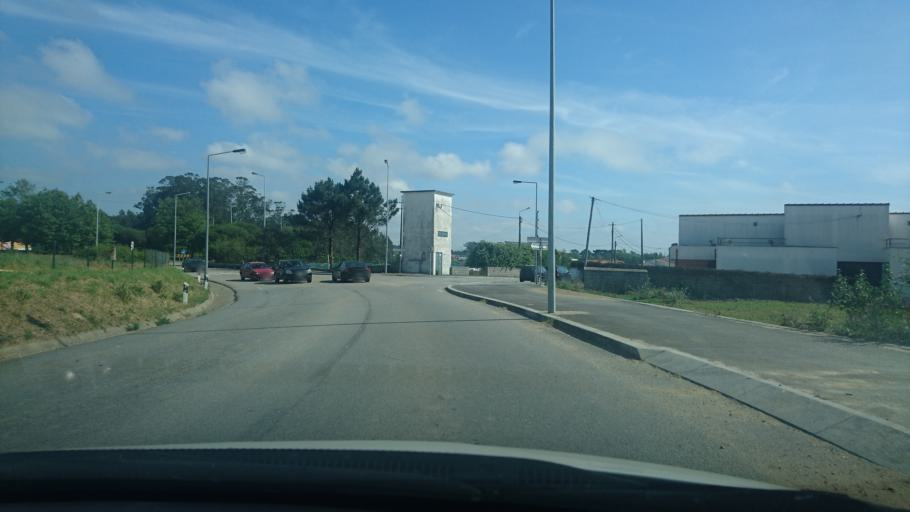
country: PT
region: Porto
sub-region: Matosinhos
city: Lavra
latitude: 41.2604
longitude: -8.7076
